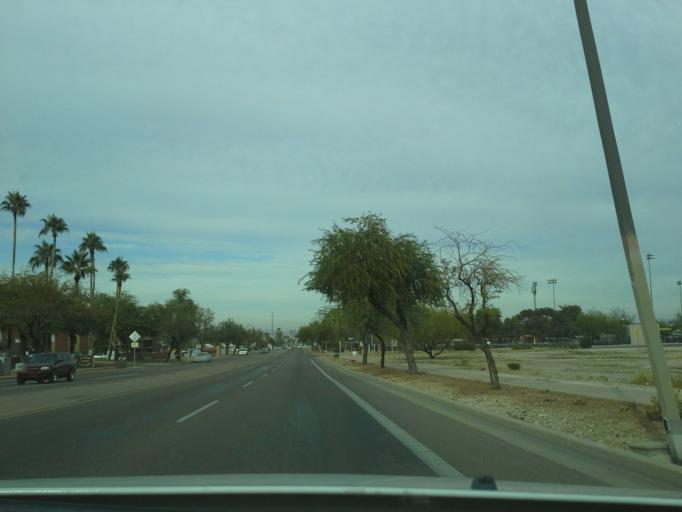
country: US
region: Arizona
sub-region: Maricopa County
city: Phoenix
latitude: 33.3729
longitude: -112.0732
